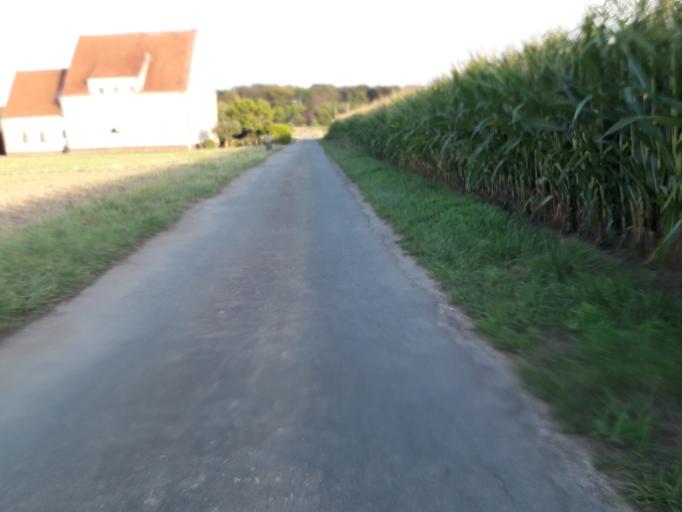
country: DE
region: North Rhine-Westphalia
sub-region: Regierungsbezirk Detmold
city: Salzkotten
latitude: 51.7055
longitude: 8.6358
